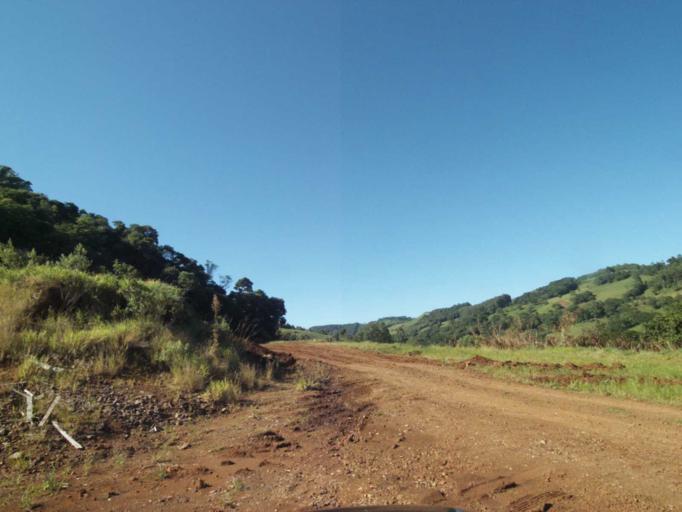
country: BR
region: Parana
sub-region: Francisco Beltrao
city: Francisco Beltrao
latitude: -26.1480
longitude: -53.3129
